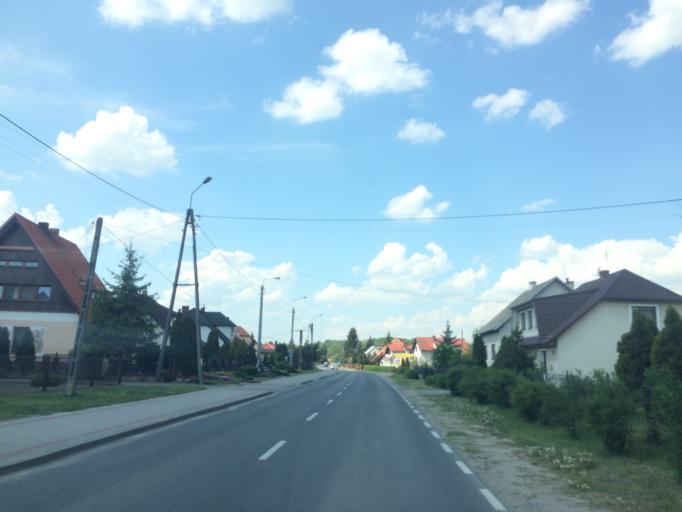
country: PL
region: Warmian-Masurian Voivodeship
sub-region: Powiat nowomiejski
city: Nowe Miasto Lubawskie
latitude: 53.4204
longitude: 19.6059
